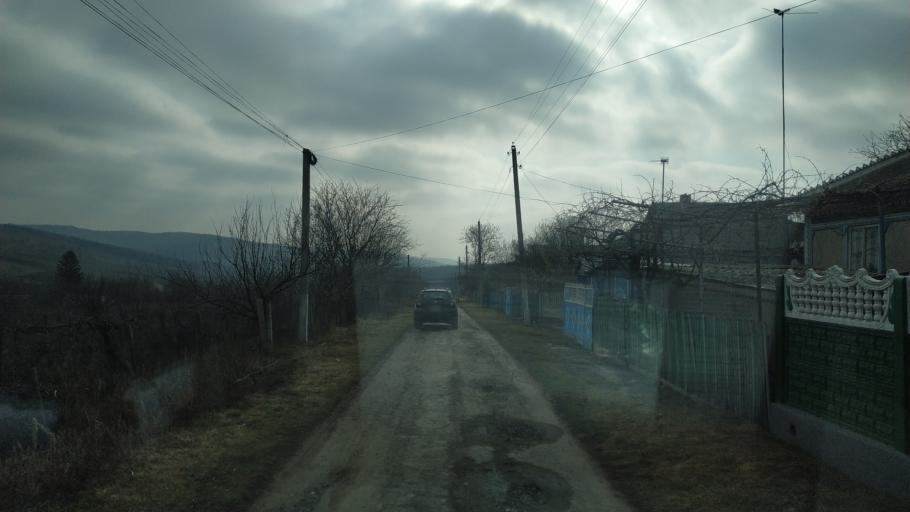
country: MD
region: Hincesti
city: Dancu
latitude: 46.8802
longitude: 28.3182
